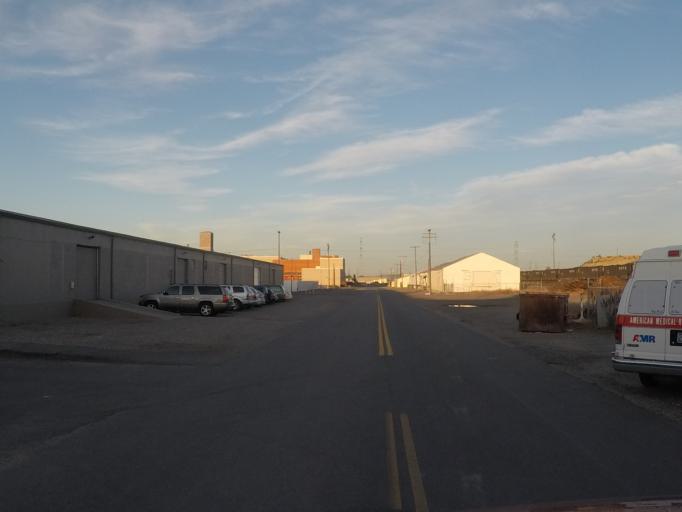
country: US
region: Montana
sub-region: Yellowstone County
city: Billings
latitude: 45.7877
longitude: -108.4915
